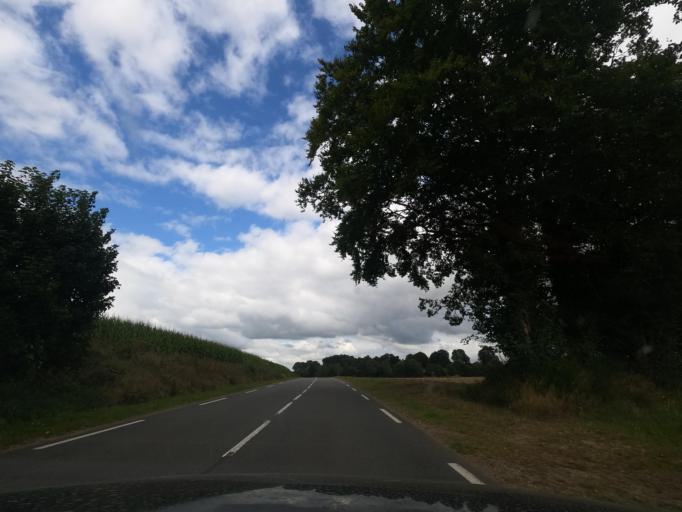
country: FR
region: Lower Normandy
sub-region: Departement de l'Orne
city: Champsecret
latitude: 48.6250
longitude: -0.5710
